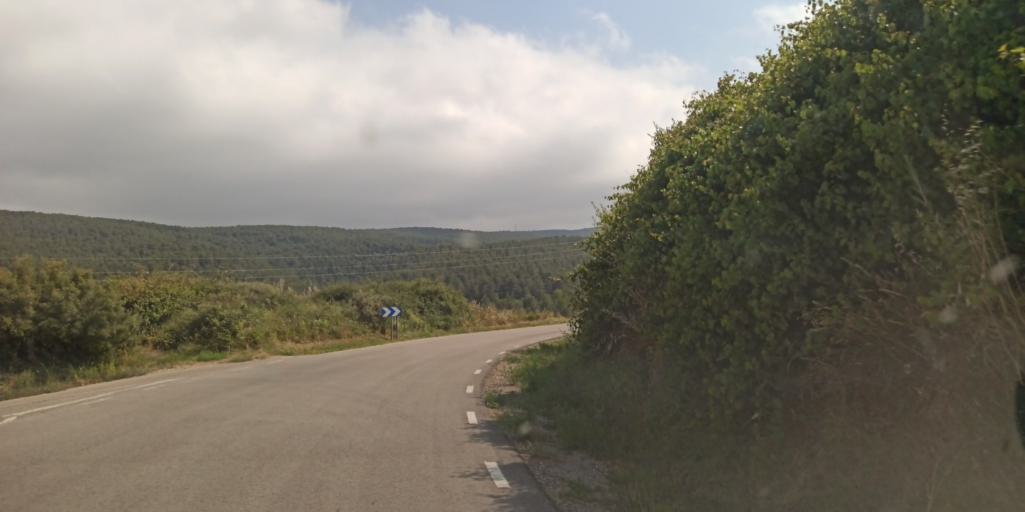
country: ES
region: Catalonia
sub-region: Provincia de Barcelona
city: Sant Joan de Mediona
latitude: 41.4744
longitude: 1.6051
